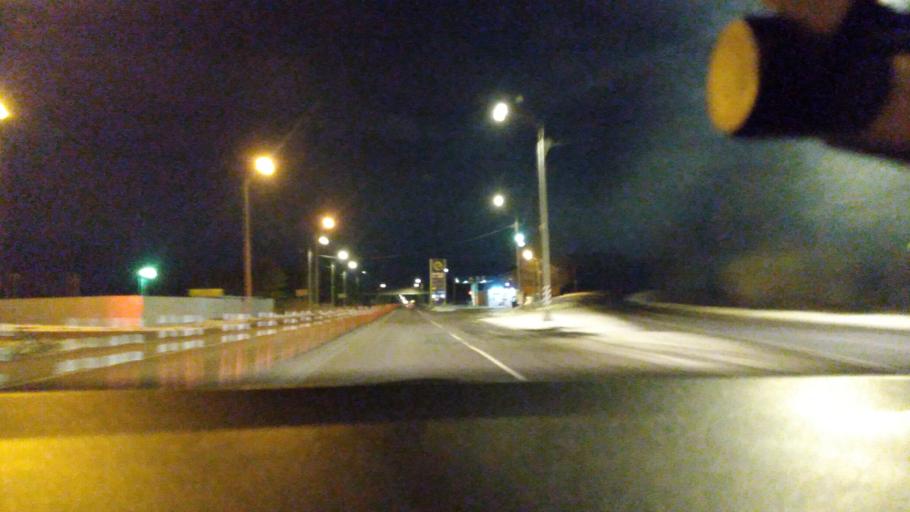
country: RU
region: Moskovskaya
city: Yegor'yevsk
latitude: 55.4179
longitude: 39.0432
